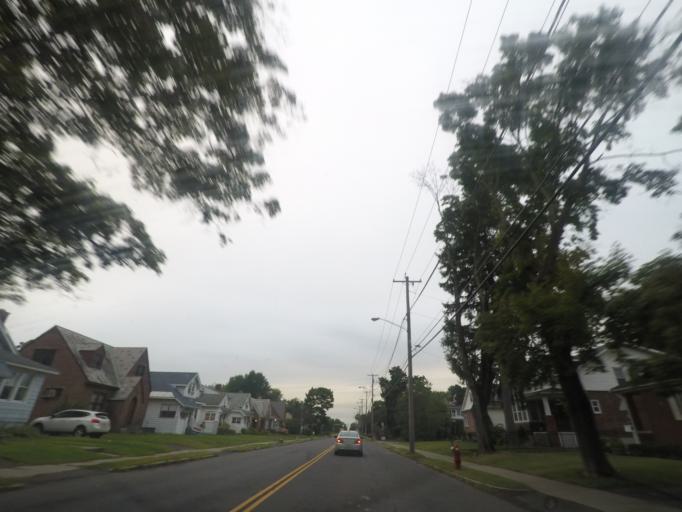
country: US
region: New York
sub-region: Albany County
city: Delmar
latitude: 42.6465
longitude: -73.7989
